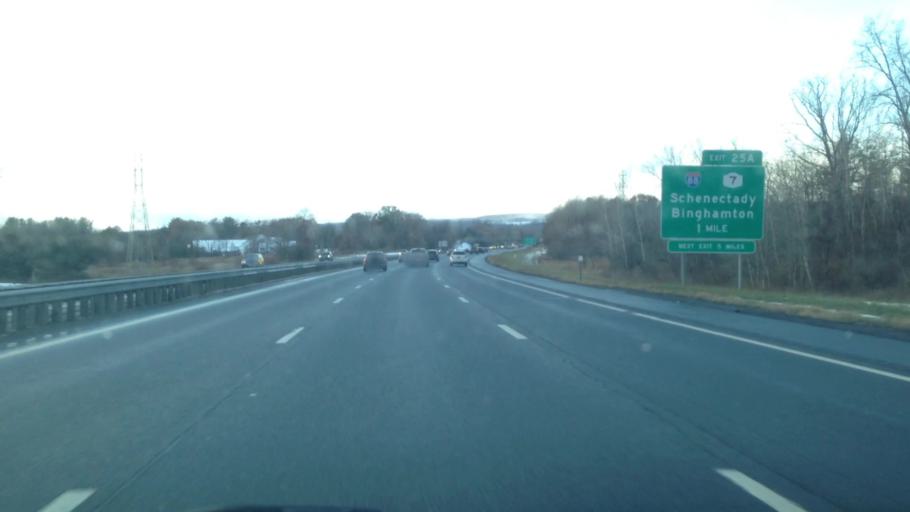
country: US
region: New York
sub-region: Schenectady County
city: Rotterdam
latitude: 42.7768
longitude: -73.9961
